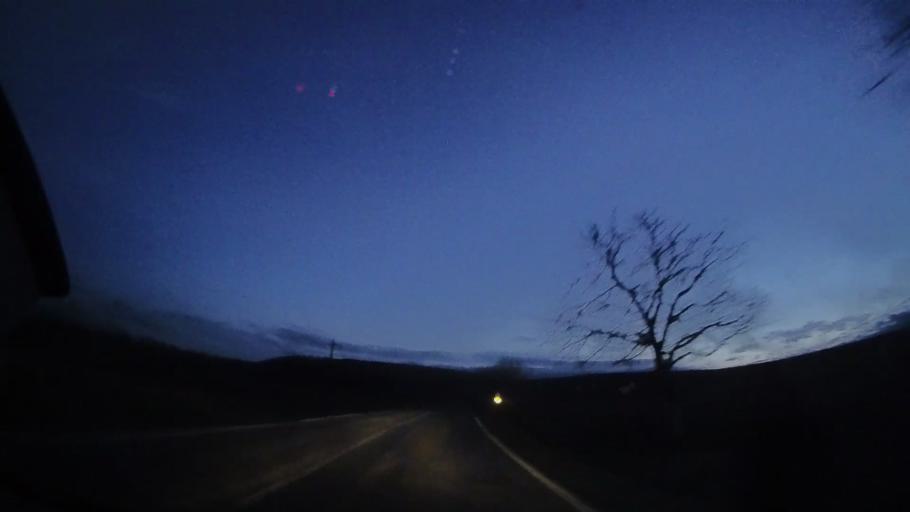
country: RO
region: Mures
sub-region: Comuna Sarmasu
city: Sarmasu
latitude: 46.7776
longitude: 24.2256
